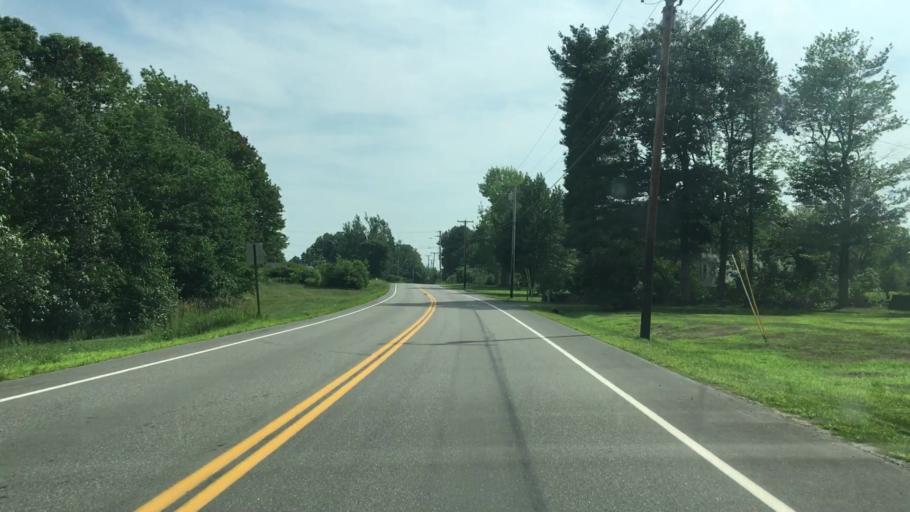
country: US
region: Maine
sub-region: Kennebec County
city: Windsor
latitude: 44.2962
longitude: -69.5850
